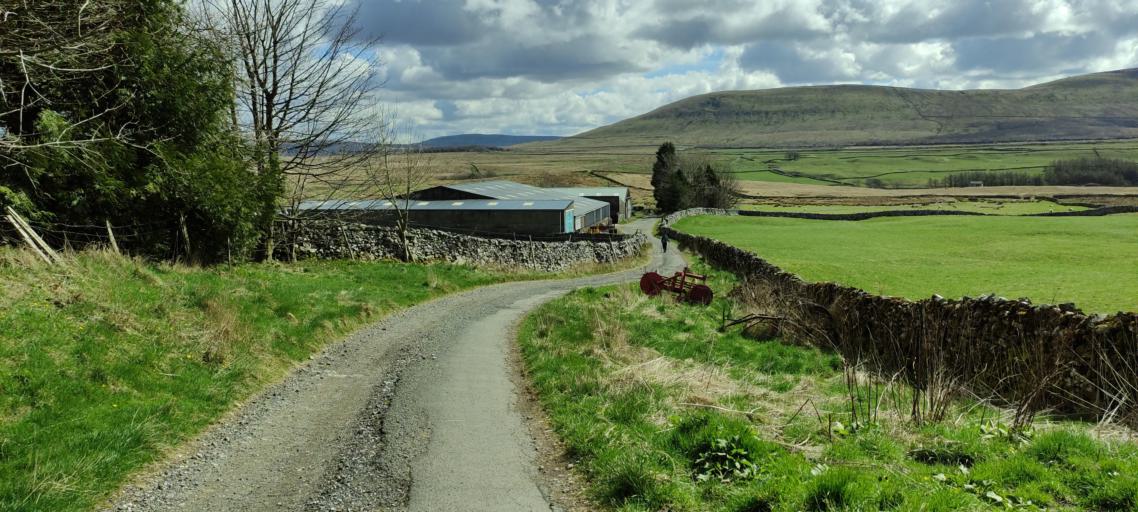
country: GB
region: England
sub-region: North Yorkshire
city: Ingleton
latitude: 54.2064
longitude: -2.4017
